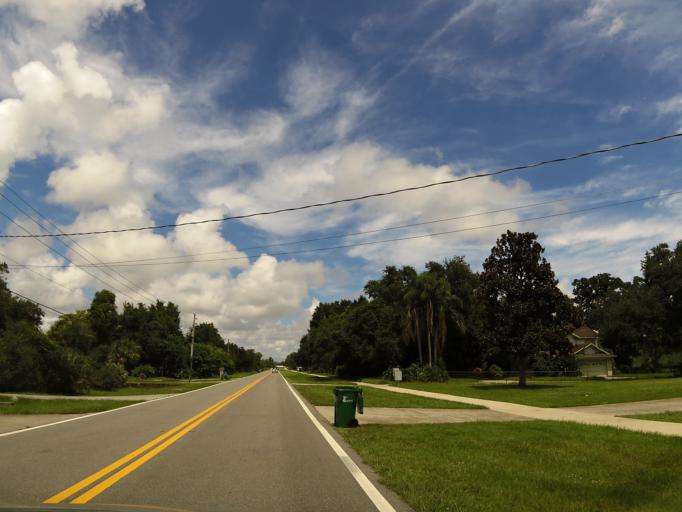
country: US
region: Florida
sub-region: Brevard County
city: Mims
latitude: 28.6311
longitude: -80.8522
